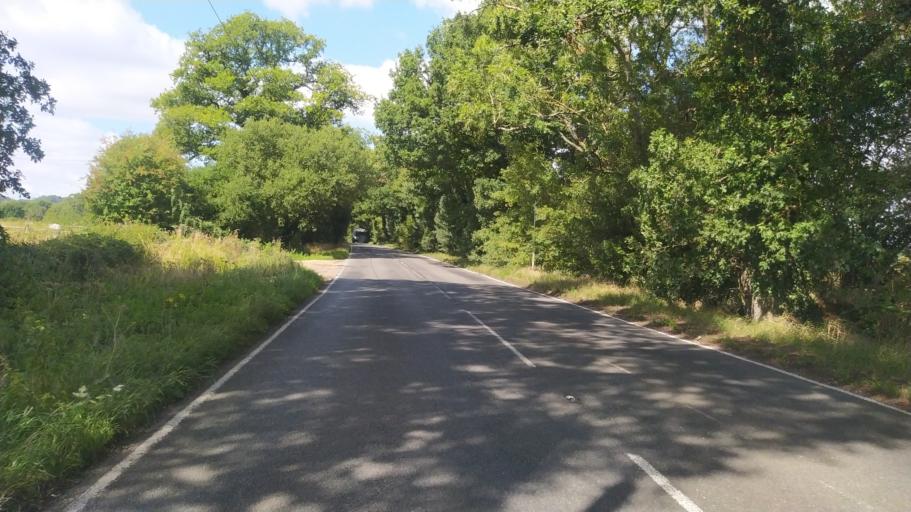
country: GB
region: England
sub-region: Hampshire
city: Kingsley
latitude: 51.1345
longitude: -0.8966
